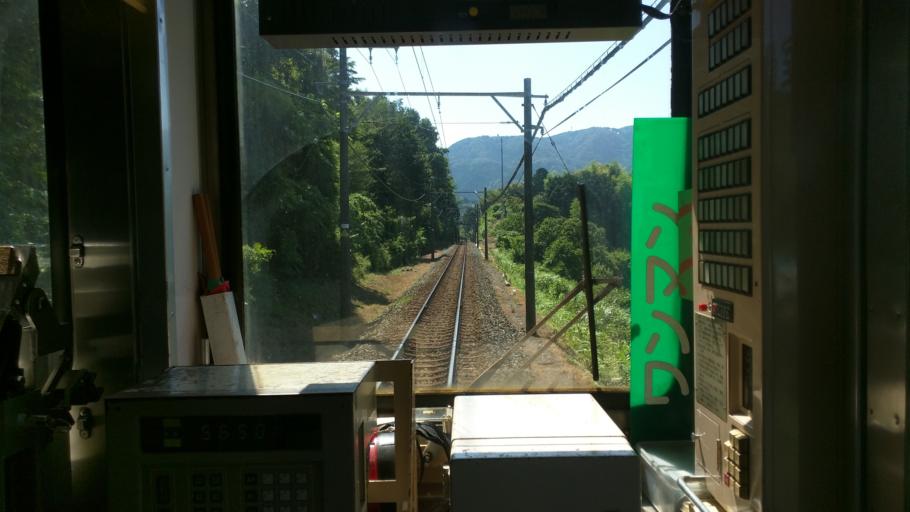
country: JP
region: Shizuoka
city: Ito
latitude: 34.9508
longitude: 139.1019
